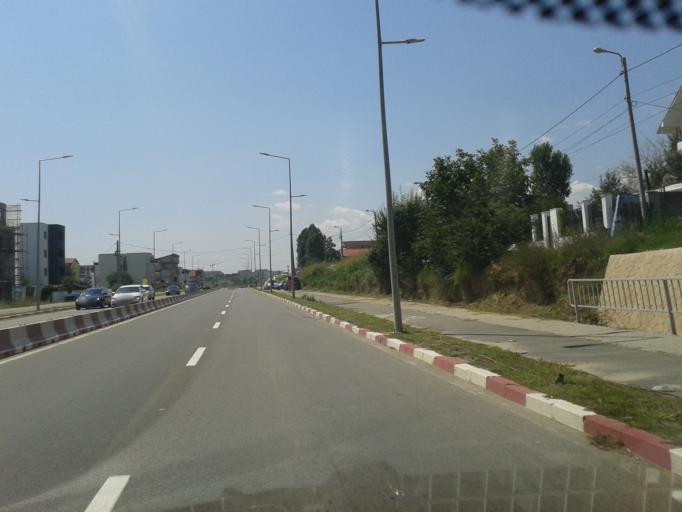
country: RO
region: Constanta
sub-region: Comuna Navodari
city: Navodari
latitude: 44.2952
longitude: 28.6193
